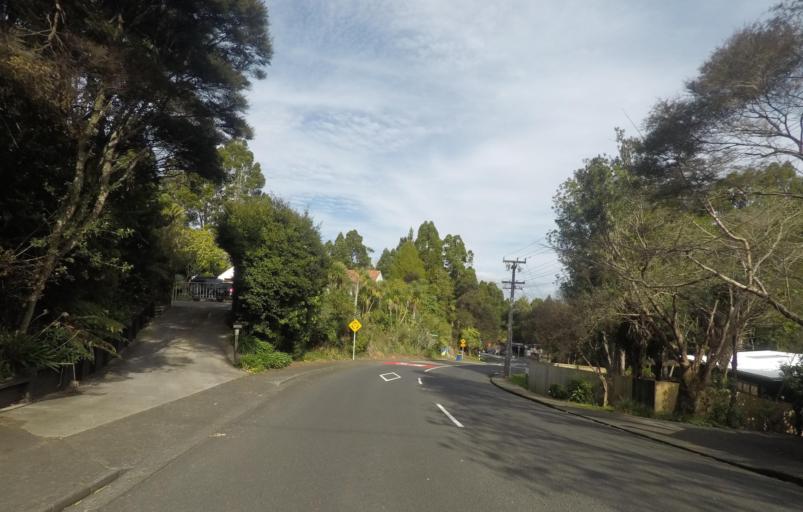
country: NZ
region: Auckland
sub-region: Auckland
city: Titirangi
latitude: -36.9394
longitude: 174.6382
